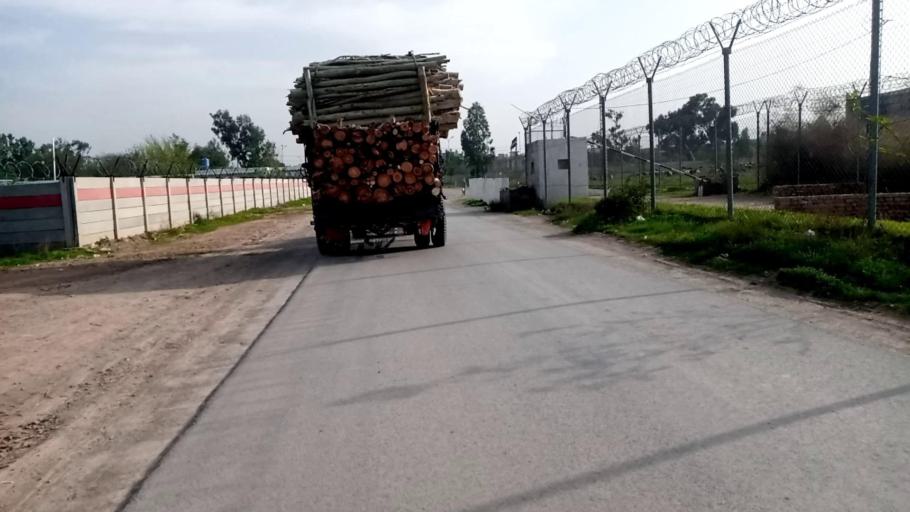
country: PK
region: Khyber Pakhtunkhwa
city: Peshawar
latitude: 33.9986
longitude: 71.4524
